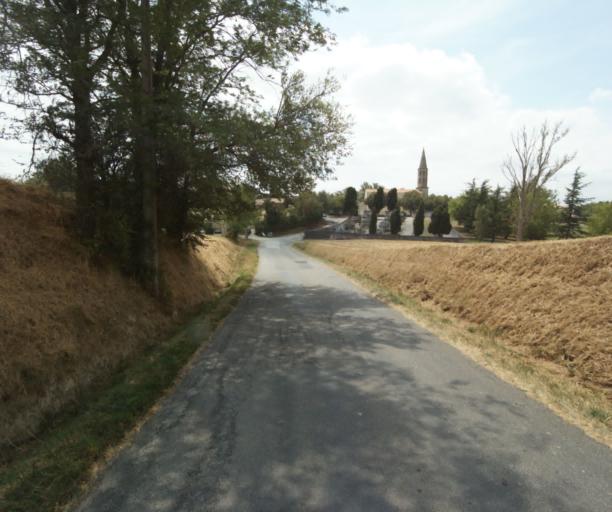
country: FR
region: Midi-Pyrenees
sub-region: Departement de la Haute-Garonne
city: Revel
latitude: 43.4374
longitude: 1.9694
